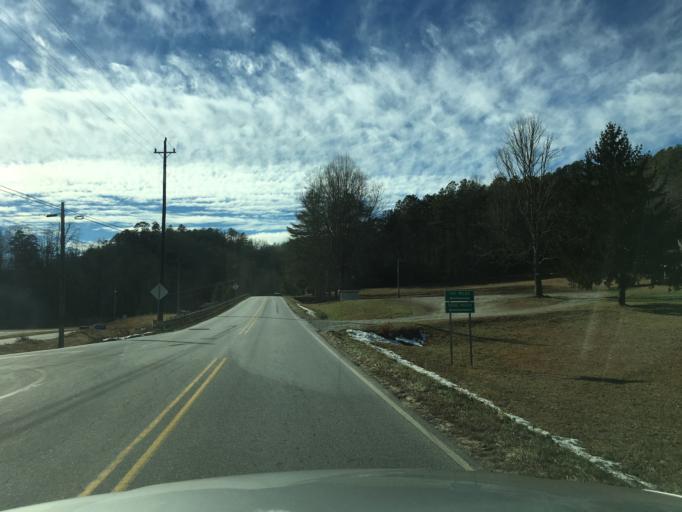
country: US
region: North Carolina
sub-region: Transylvania County
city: Brevard
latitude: 35.1390
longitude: -82.8516
